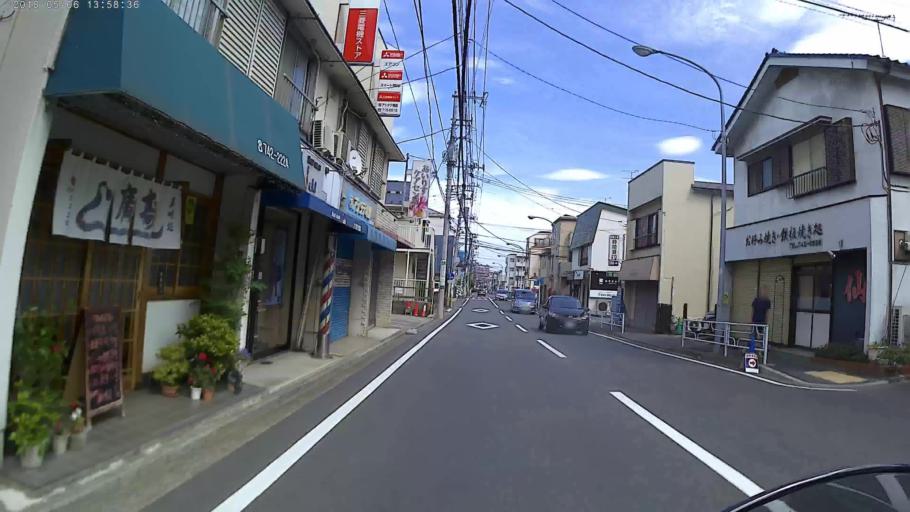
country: JP
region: Kanagawa
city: Yokohama
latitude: 35.4389
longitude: 139.5917
